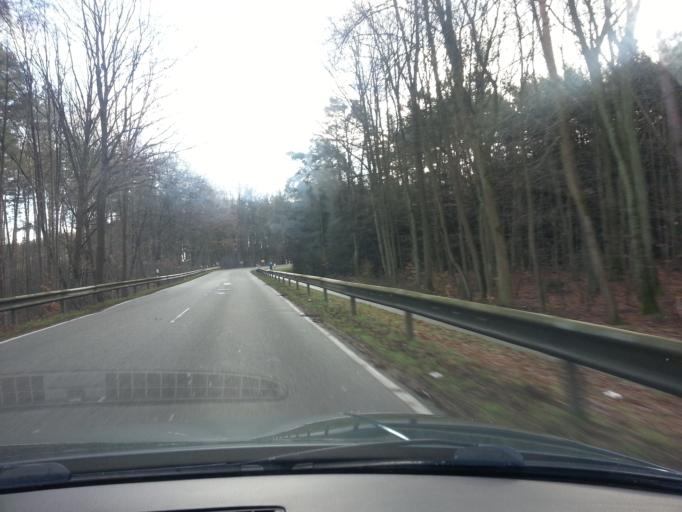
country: DE
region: Rheinland-Pfalz
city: Rodenbach
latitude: 49.4710
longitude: 7.6724
